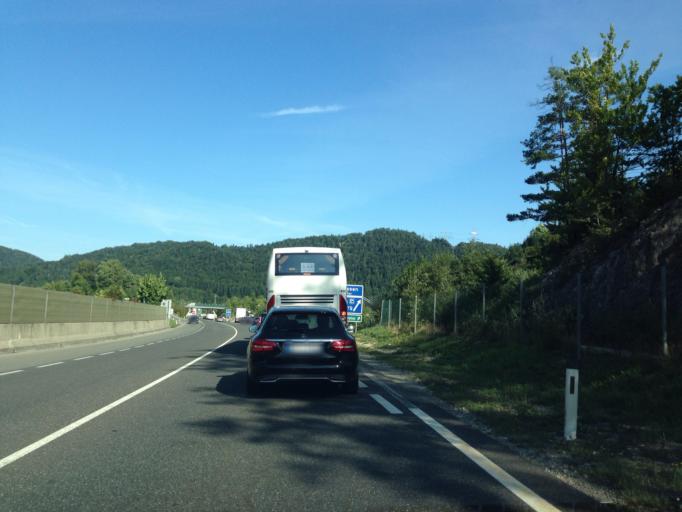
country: AT
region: Tyrol
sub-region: Politischer Bezirk Reutte
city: Musau
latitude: 47.5456
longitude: 10.6623
